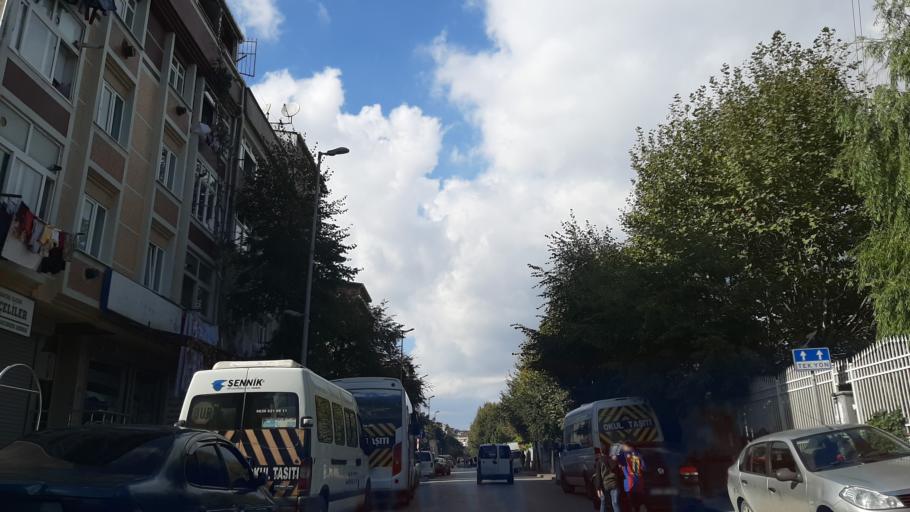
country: TR
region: Istanbul
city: Esenyurt
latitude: 41.0339
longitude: 28.6600
